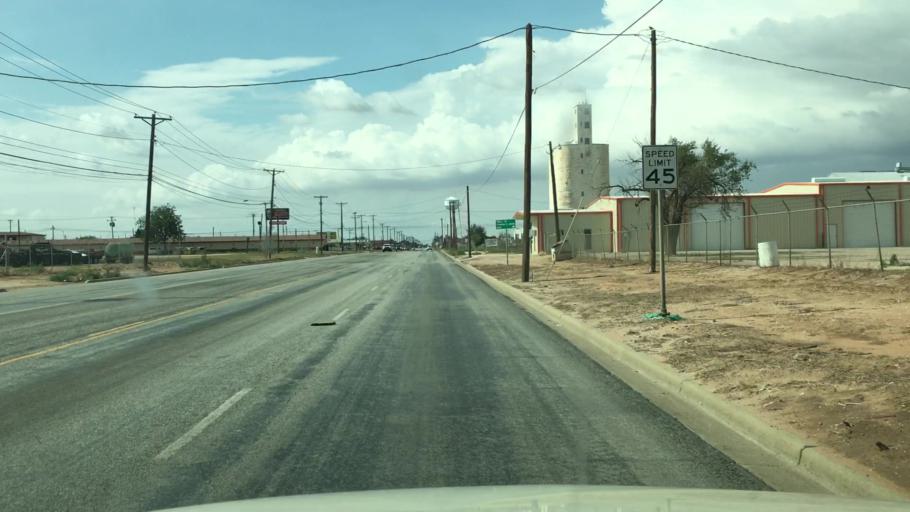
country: US
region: Texas
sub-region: Dawson County
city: Lamesa
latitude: 32.7241
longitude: -101.9464
